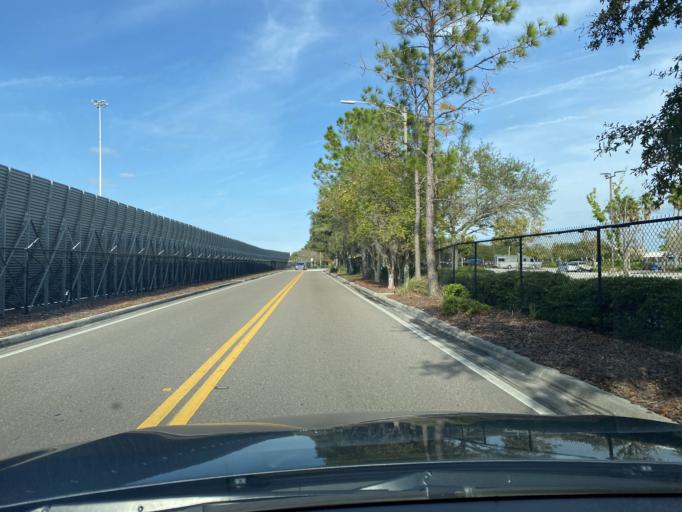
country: US
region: Florida
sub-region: Orange County
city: Belle Isle
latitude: 28.4490
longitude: -81.3151
